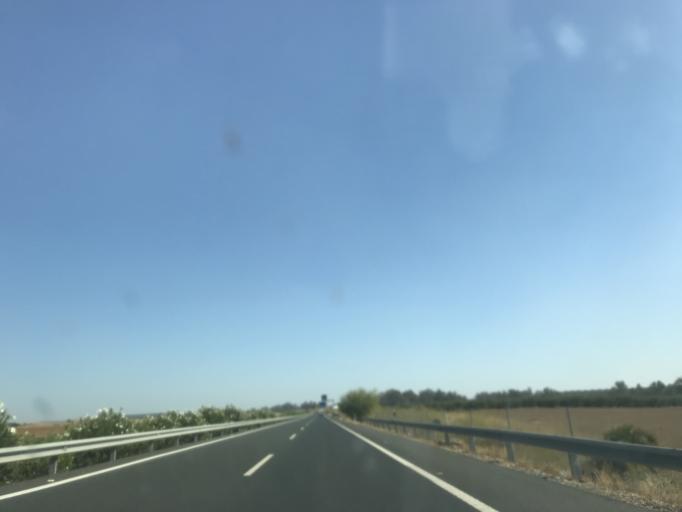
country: ES
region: Andalusia
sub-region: Provincia de Sevilla
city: Mairena del Alcor
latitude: 37.3092
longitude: -5.7440
